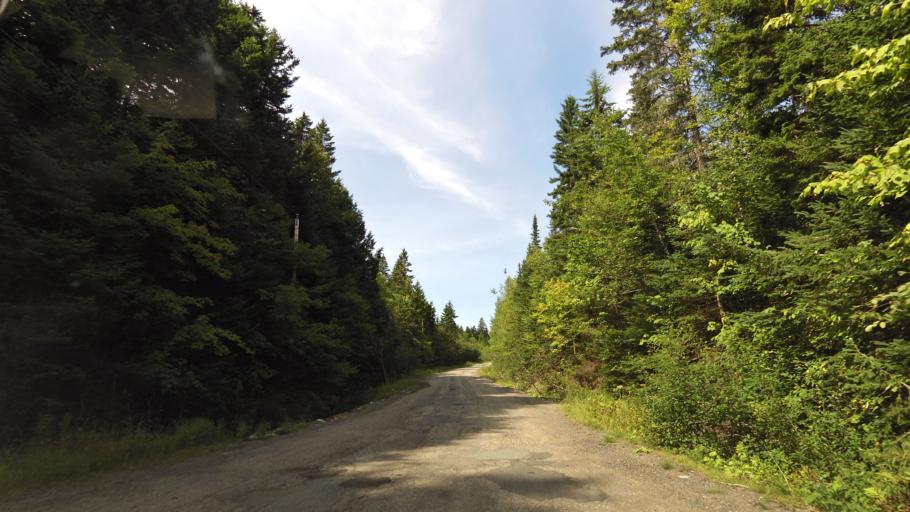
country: CA
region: New Brunswick
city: Hampton
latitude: 45.5554
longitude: -65.8418
